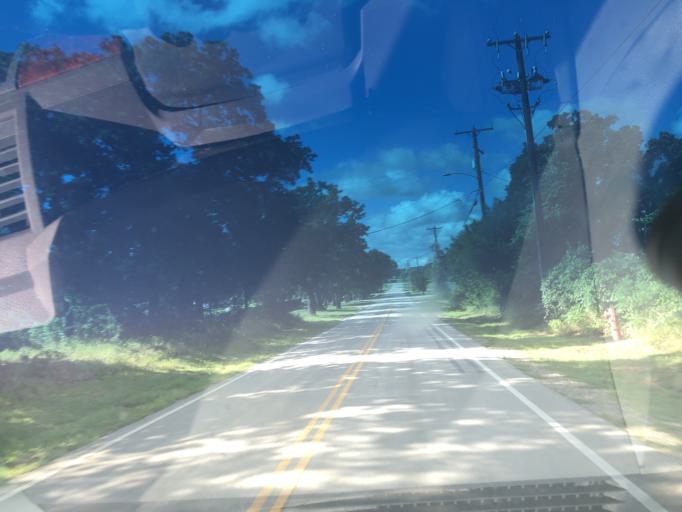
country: US
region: Texas
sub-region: Dallas County
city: Grand Prairie
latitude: 32.7966
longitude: -97.0204
